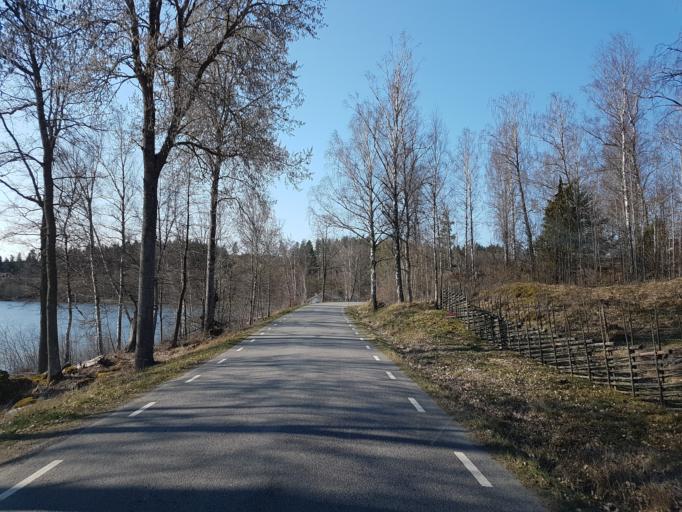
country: SE
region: OEstergoetland
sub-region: Valdemarsviks Kommun
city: Gusum
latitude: 58.1930
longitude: 16.3158
